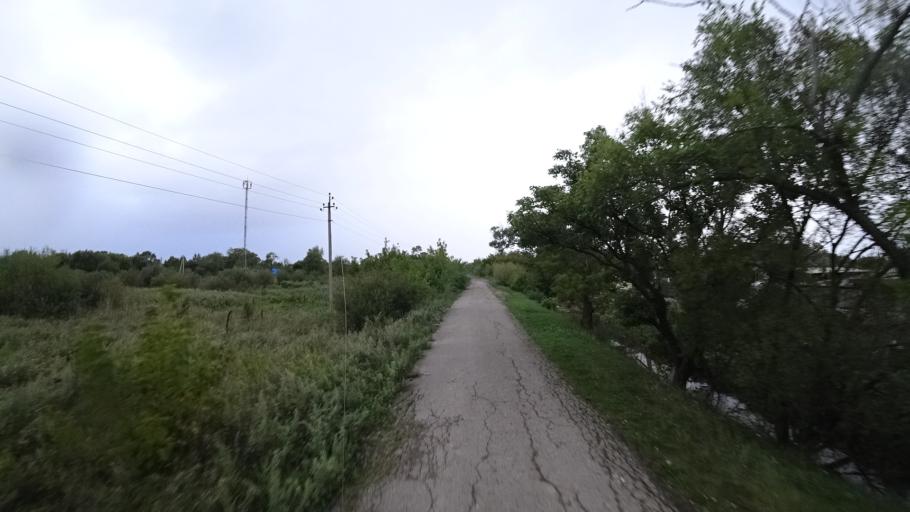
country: RU
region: Primorskiy
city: Chernigovka
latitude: 44.4014
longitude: 132.5315
